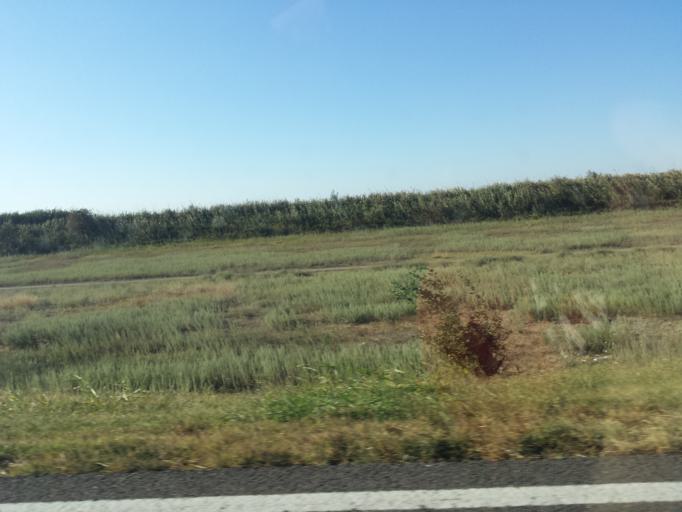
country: RO
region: Ialomita
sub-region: Comuna Cosambesti
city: Cosambesti
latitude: 44.5860
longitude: 27.4335
